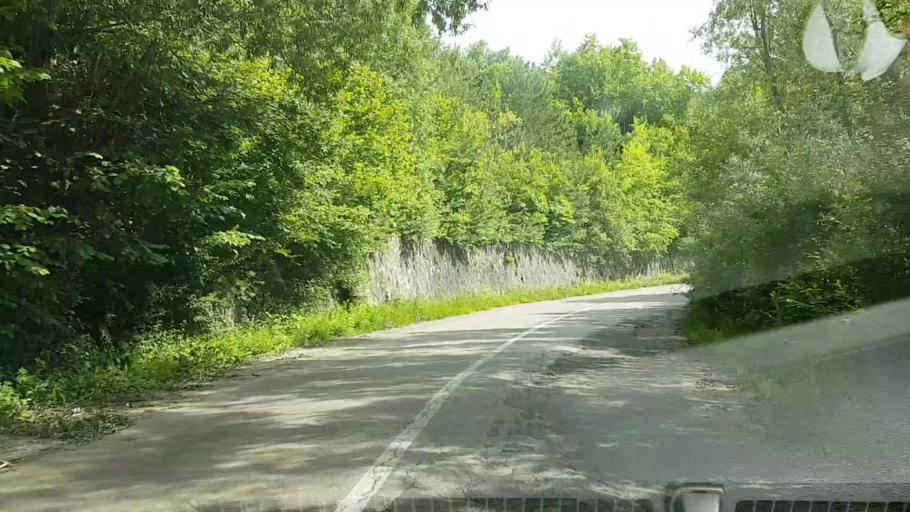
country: RO
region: Neamt
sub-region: Comuna Hangu
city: Hangu
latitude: 47.0279
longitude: 26.0683
